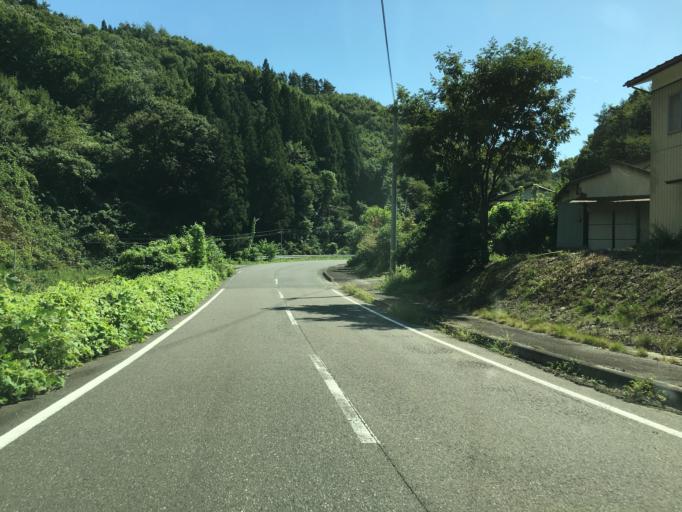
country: JP
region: Fukushima
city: Sukagawa
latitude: 37.2972
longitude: 140.4896
